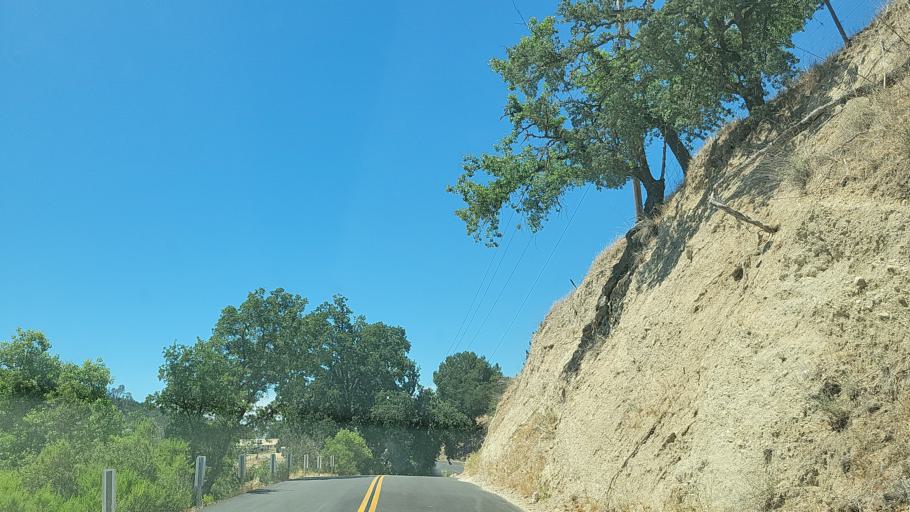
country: US
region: California
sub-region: San Luis Obispo County
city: Atascadero
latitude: 35.4900
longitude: -120.6396
